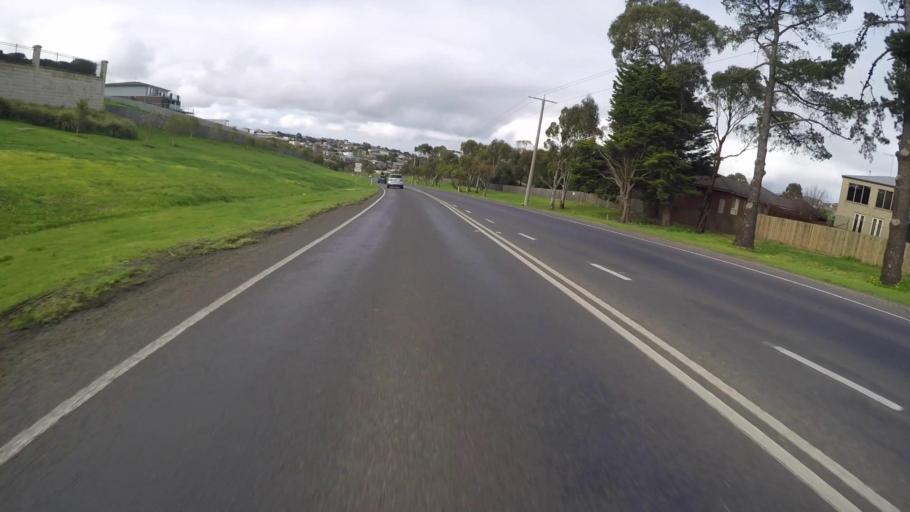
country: AU
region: Victoria
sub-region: Greater Geelong
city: Wandana Heights
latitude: -38.1705
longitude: 144.3015
